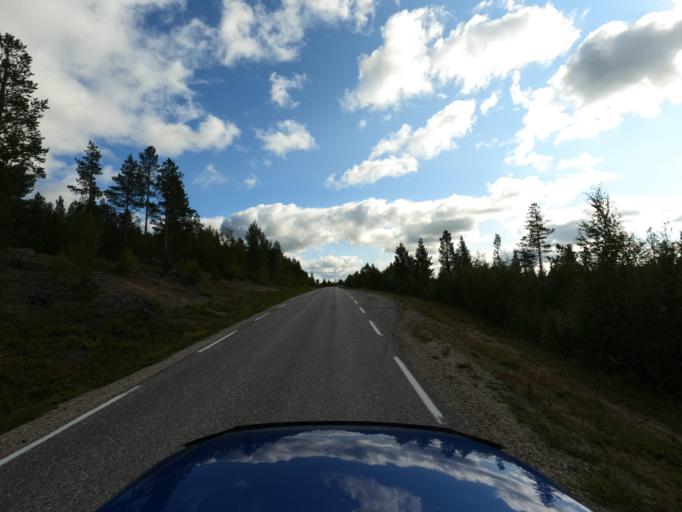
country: NO
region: Finnmark Fylke
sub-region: Karasjok
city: Karasjohka
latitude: 69.4433
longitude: 25.2486
